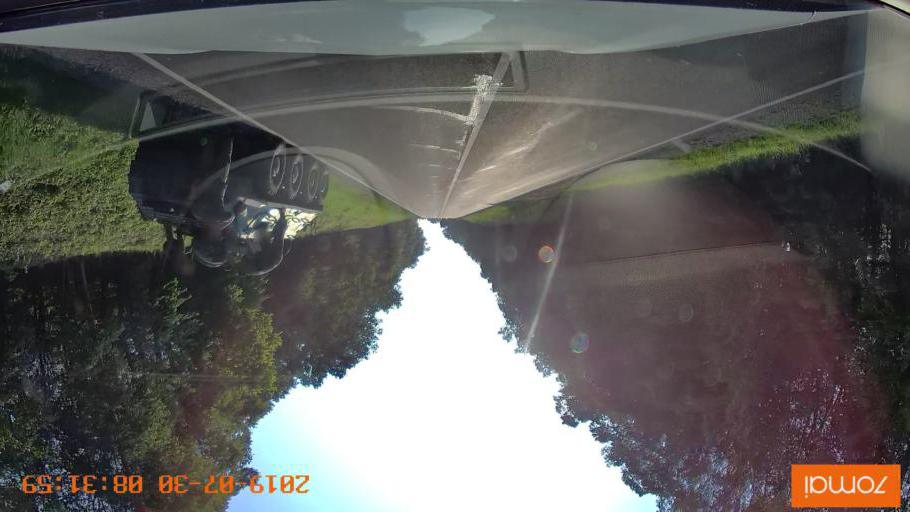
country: RU
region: Kaliningrad
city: Chernyakhovsk
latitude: 54.6387
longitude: 21.7191
